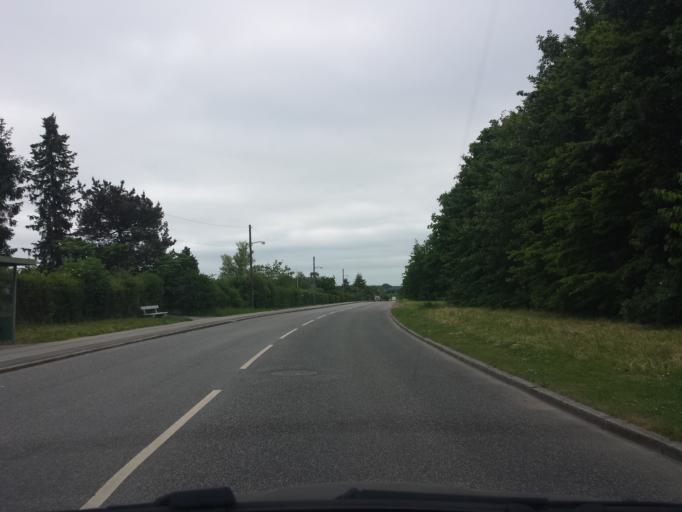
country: DK
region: Capital Region
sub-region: Ballerup Kommune
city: Ballerup
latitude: 55.7116
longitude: 12.3821
